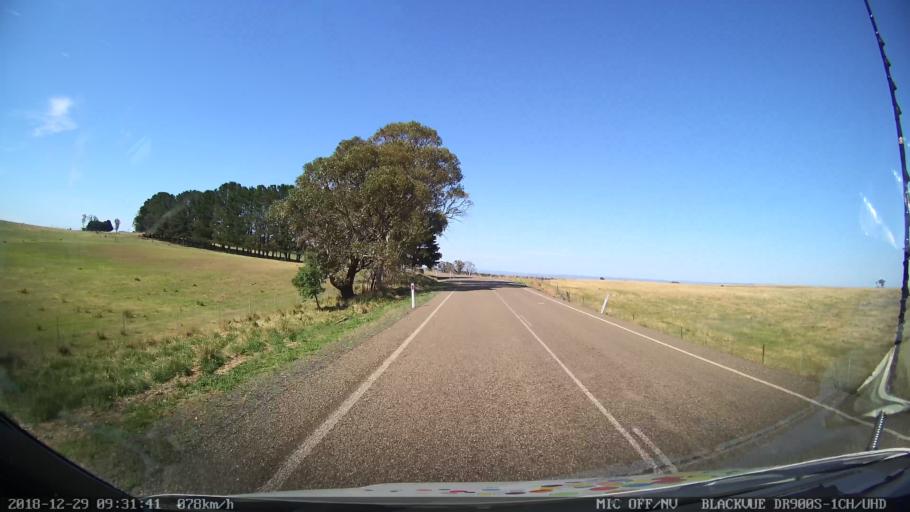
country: AU
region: New South Wales
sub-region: Upper Lachlan Shire
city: Crookwell
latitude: -34.6093
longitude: 149.3600
